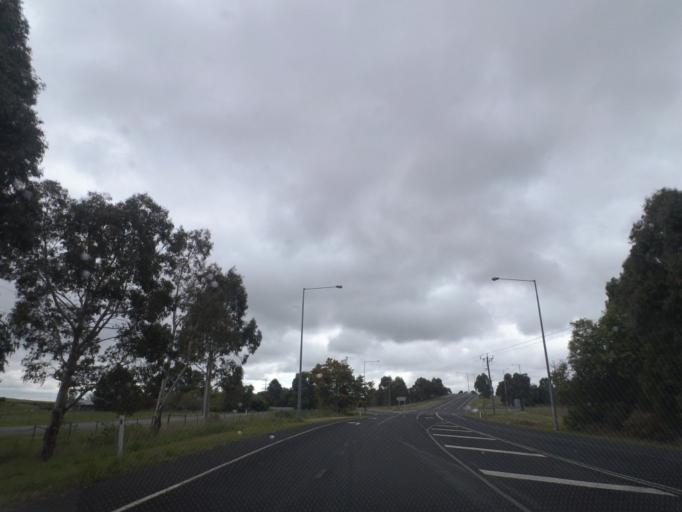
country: AU
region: Victoria
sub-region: Hume
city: Sunbury
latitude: -37.3233
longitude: 144.5239
